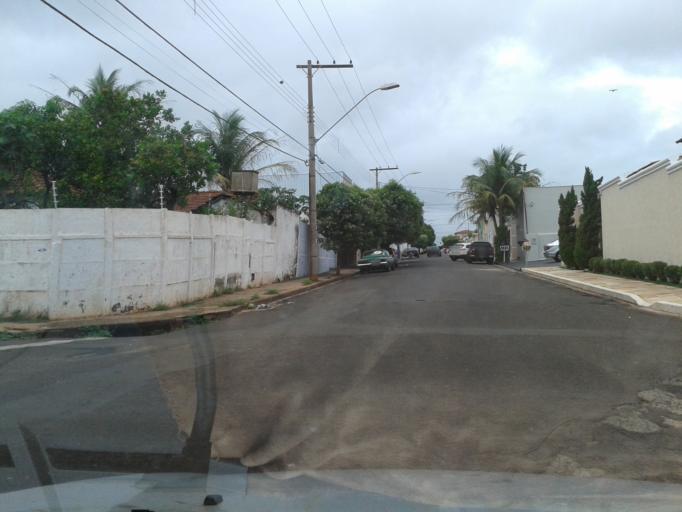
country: BR
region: Minas Gerais
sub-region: Ituiutaba
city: Ituiutaba
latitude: -18.9792
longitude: -49.4651
